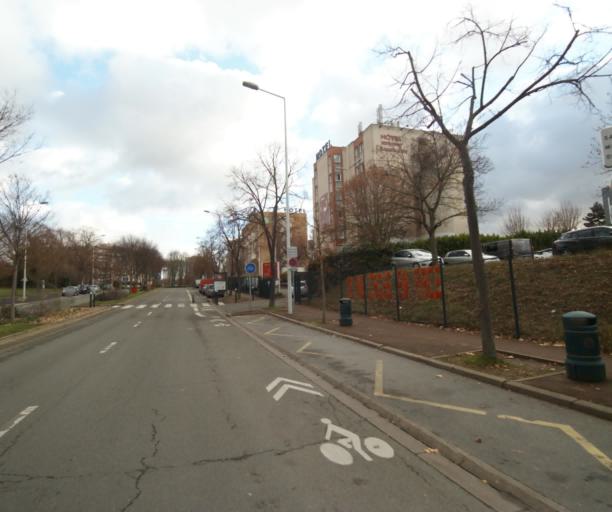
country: FR
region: Ile-de-France
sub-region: Departement des Hauts-de-Seine
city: Nanterre
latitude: 48.8928
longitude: 2.2132
